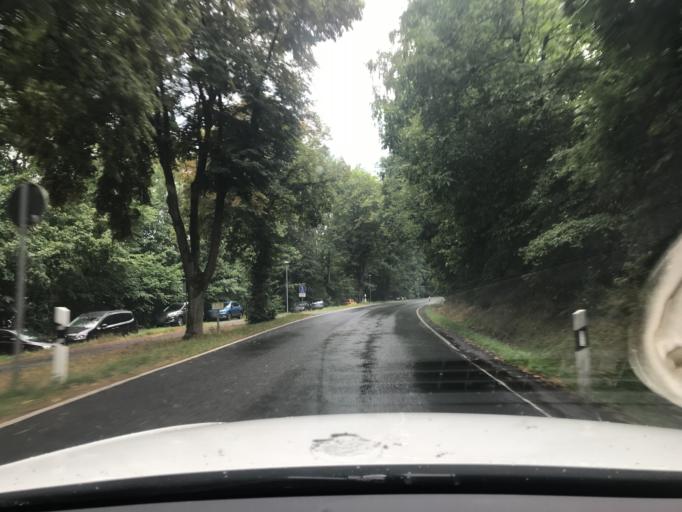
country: DE
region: Bavaria
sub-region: Upper Palatinate
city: Speinshart
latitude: 49.7563
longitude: 11.8101
